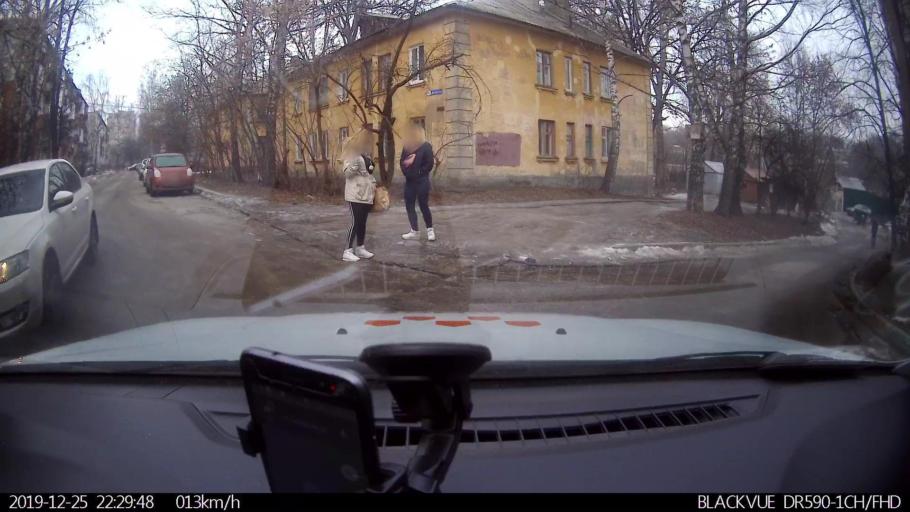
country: RU
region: Nizjnij Novgorod
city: Nizhniy Novgorod
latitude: 56.2698
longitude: 43.9851
